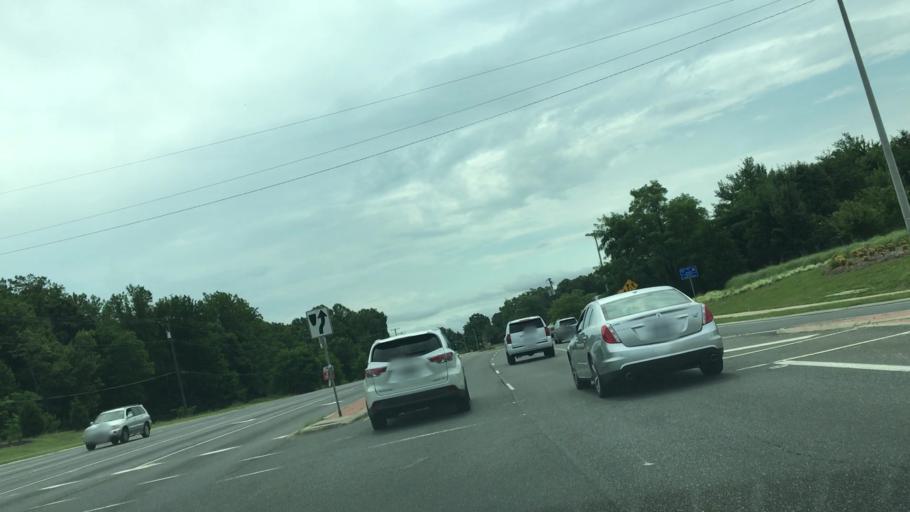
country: US
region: Virginia
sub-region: Prince William County
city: Lake Ridge
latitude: 38.6810
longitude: -77.3599
